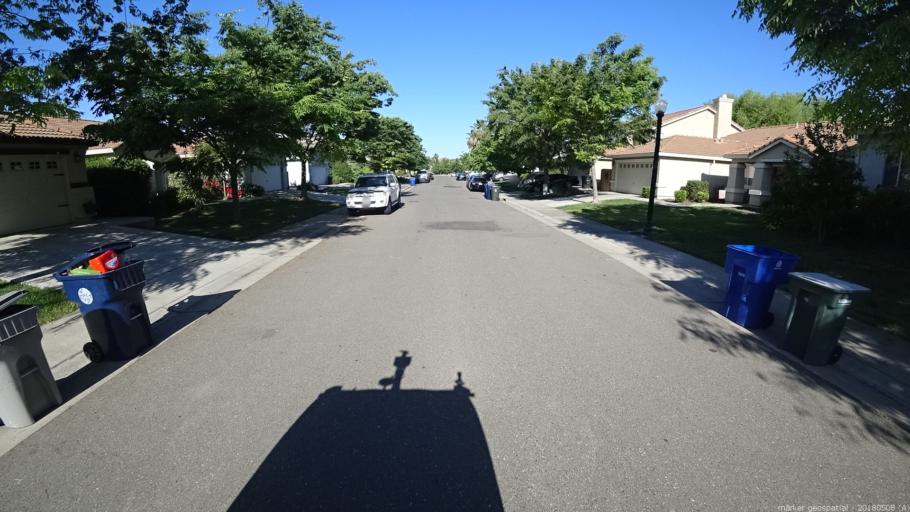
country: US
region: California
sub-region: Sacramento County
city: Elverta
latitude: 38.6780
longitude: -121.5051
